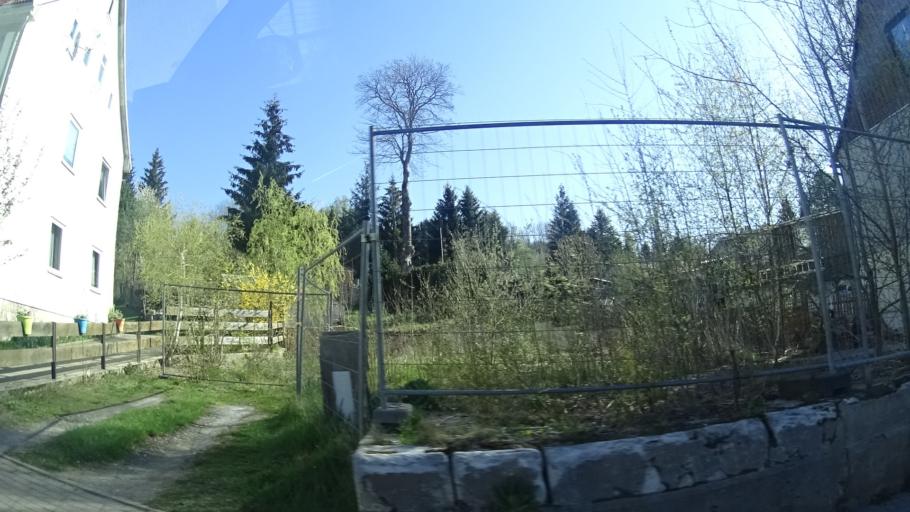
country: DE
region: Thuringia
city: Bohlen
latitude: 50.5871
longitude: 11.0455
